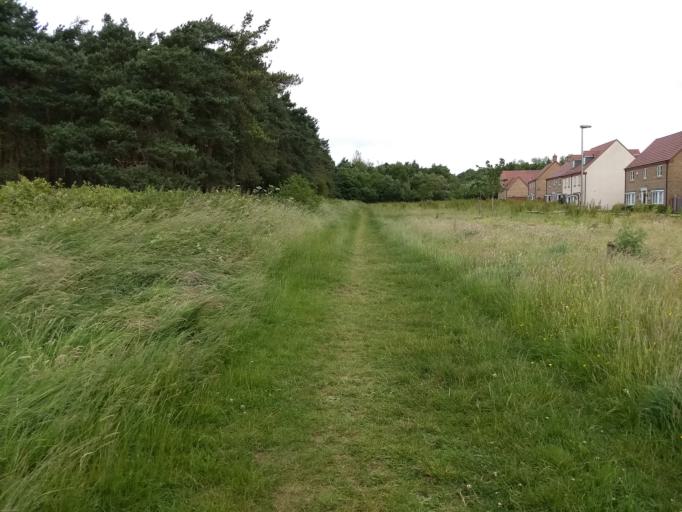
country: GB
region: England
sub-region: Milton Keynes
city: Shenley Church End
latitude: 52.0086
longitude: -0.8119
